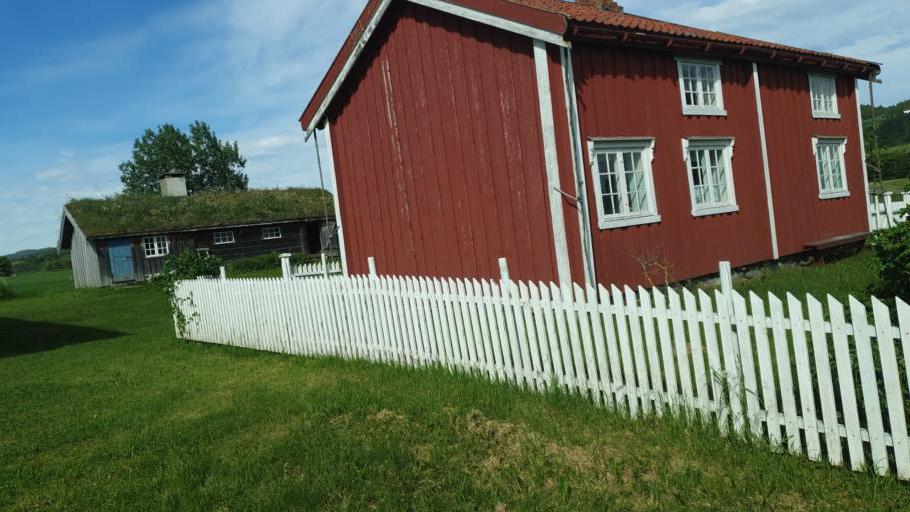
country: NO
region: Sor-Trondelag
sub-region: Rissa
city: Rissa
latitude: 63.4959
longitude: 10.0157
